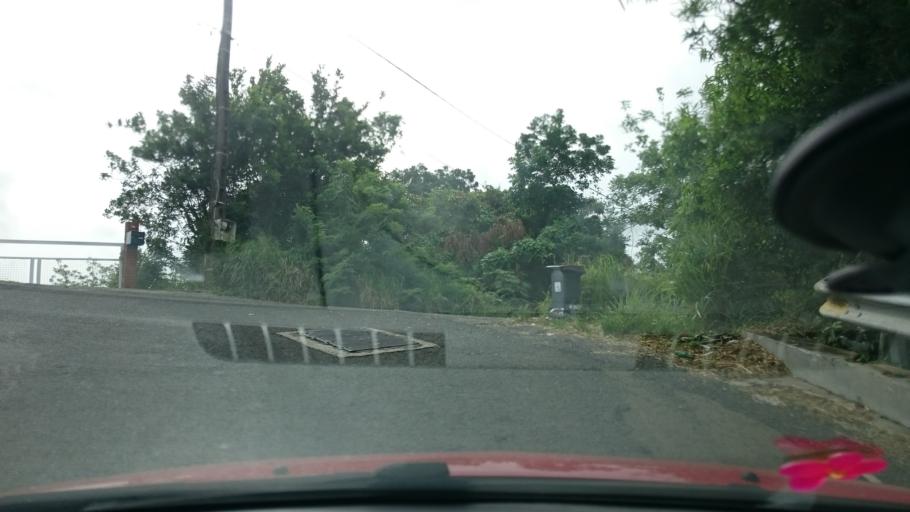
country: MQ
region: Martinique
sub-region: Martinique
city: Sainte-Luce
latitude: 14.4863
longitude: -60.9234
